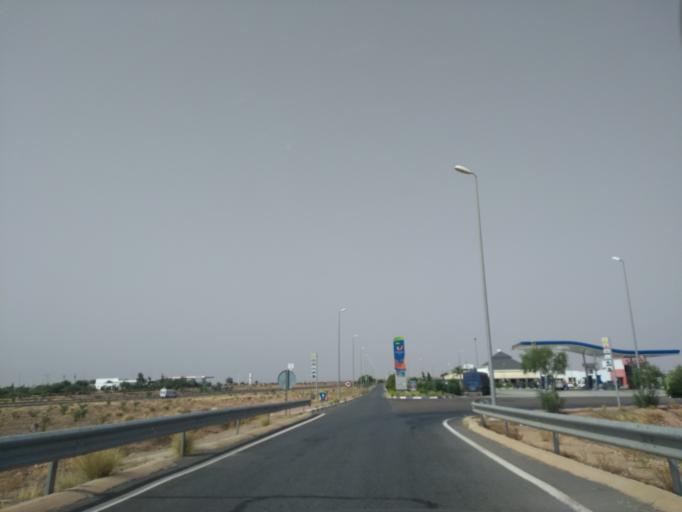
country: MA
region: Marrakech-Tensift-Al Haouz
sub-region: Marrakech
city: Marrakesh
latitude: 31.7208
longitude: -8.2332
